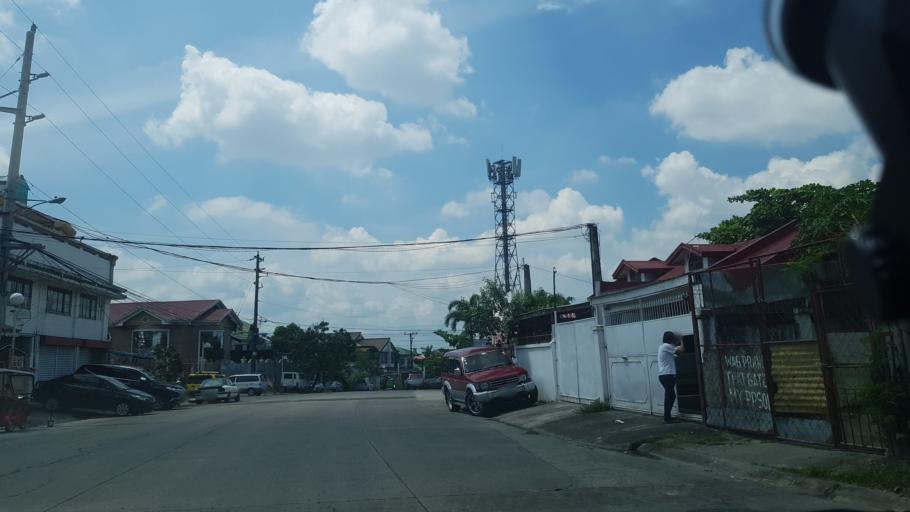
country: PH
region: Calabarzon
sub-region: Province of Rizal
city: Las Pinas
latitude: 14.4296
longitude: 120.9895
